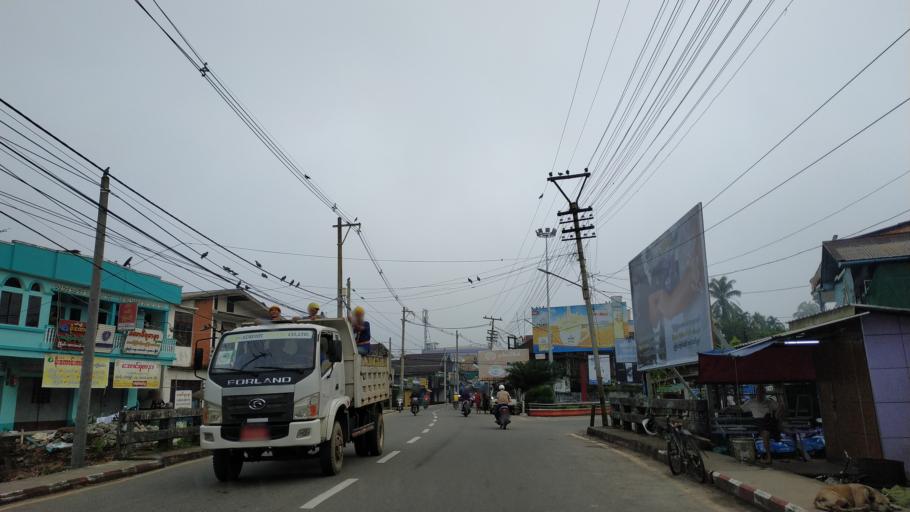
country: MM
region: Tanintharyi
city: Dawei
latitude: 14.0764
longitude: 98.1932
